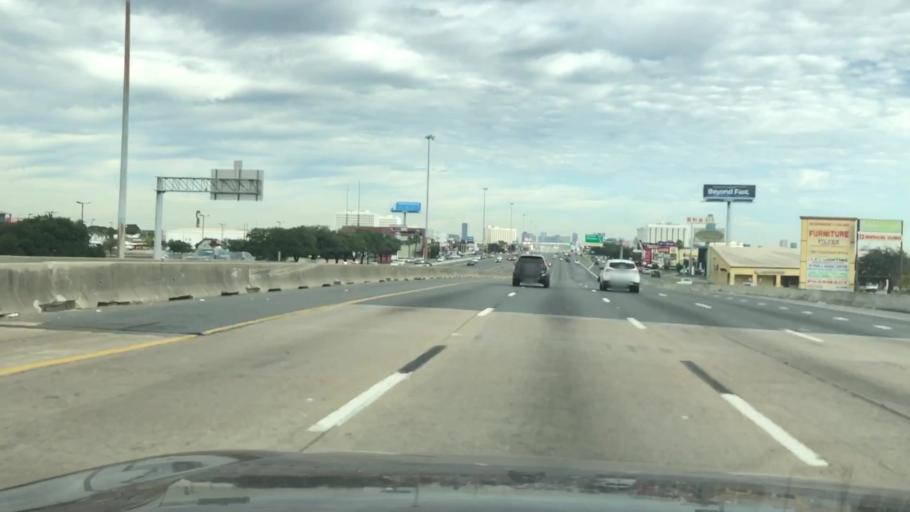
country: US
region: Texas
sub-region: Harris County
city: Bellaire
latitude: 29.7049
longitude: -95.5124
